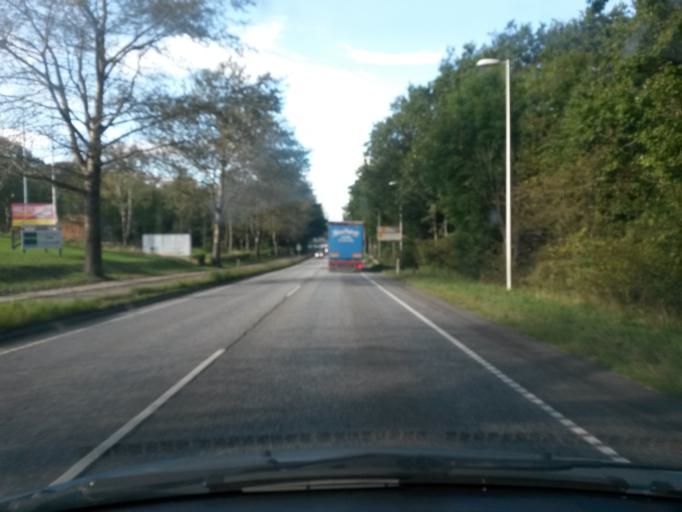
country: DK
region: Central Jutland
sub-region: Holstebro Kommune
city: Holstebro
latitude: 56.3439
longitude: 8.6344
